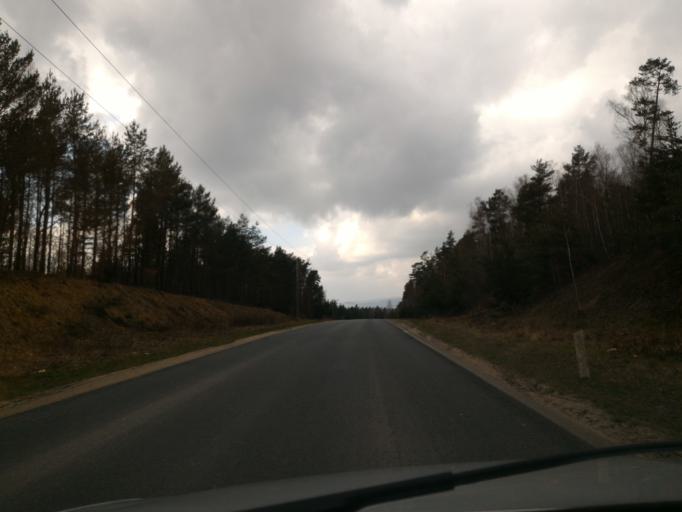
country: CZ
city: Hradek nad Nisou
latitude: 50.8767
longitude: 14.8978
